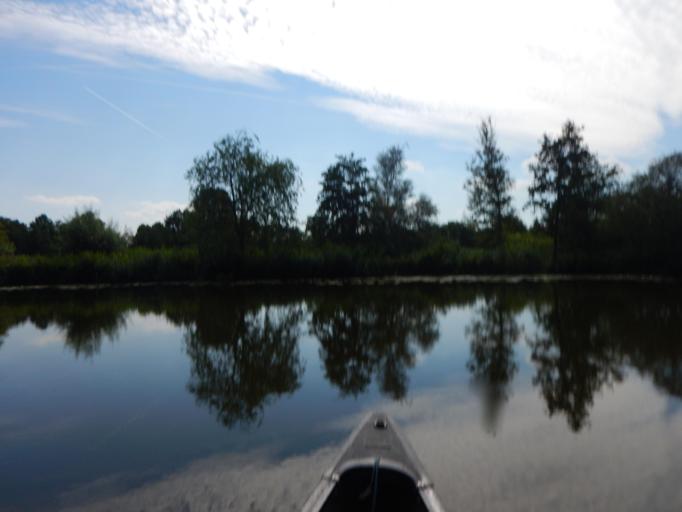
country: NL
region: North Holland
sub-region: Gemeente Wijdemeren
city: Kortenhoef
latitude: 52.2736
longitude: 5.1033
